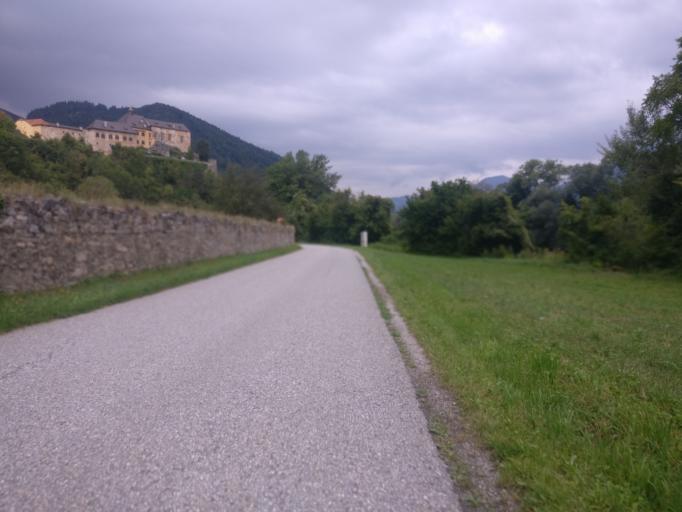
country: AT
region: Styria
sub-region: Politischer Bezirk Graz-Umgebung
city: Frohnleiten
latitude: 47.2439
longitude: 15.3111
